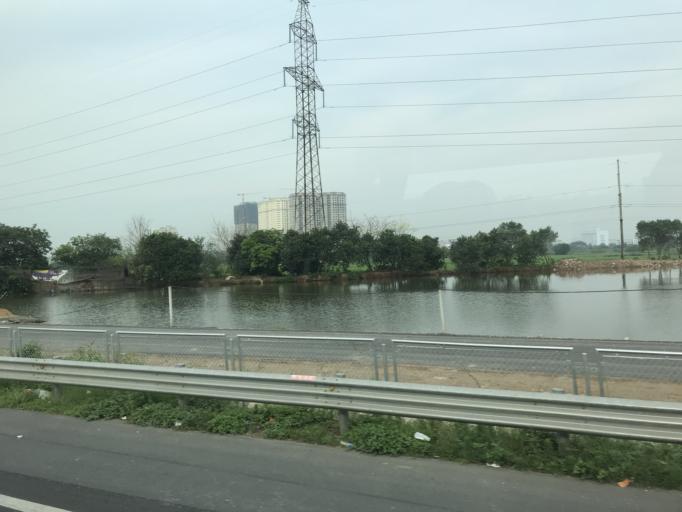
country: VN
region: Ha Noi
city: Van Dien
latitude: 20.9365
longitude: 105.8591
